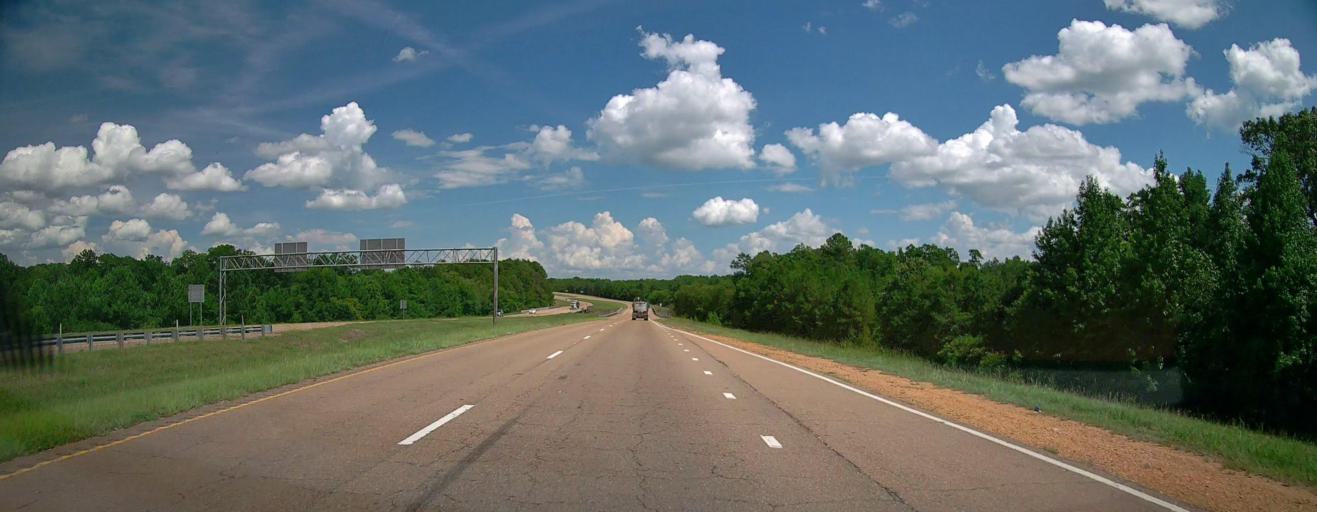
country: US
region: Mississippi
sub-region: Monroe County
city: Aberdeen
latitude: 33.8122
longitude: -88.4892
